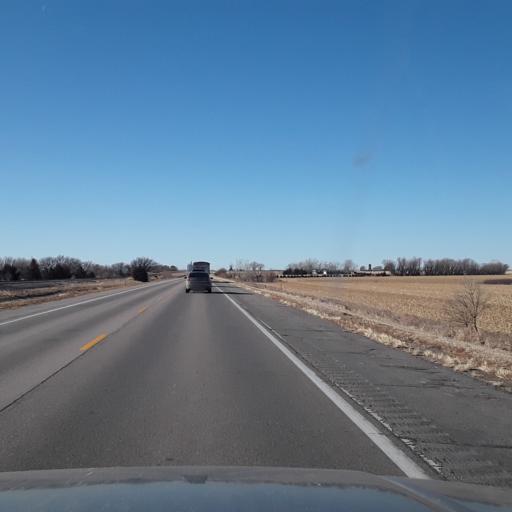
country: US
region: Nebraska
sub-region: Kearney County
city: Minden
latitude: 40.5000
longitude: -98.9707
